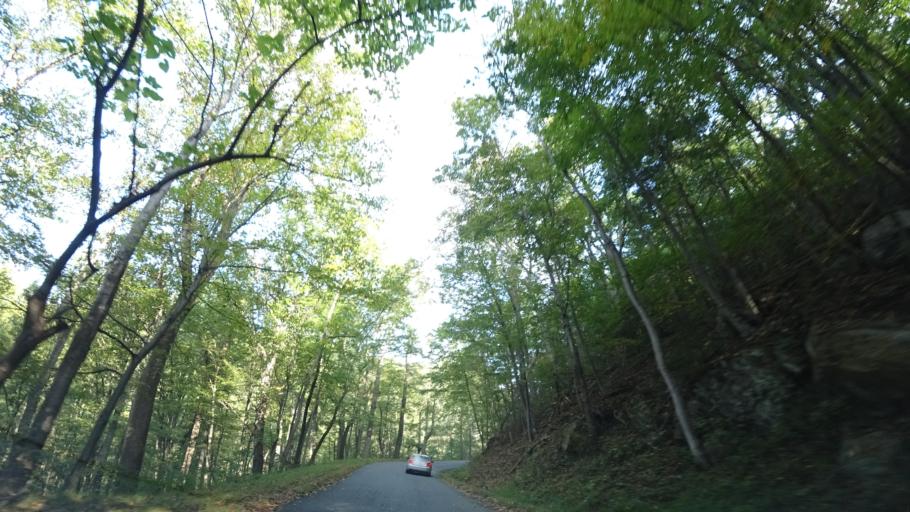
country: US
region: Virginia
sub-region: Madison County
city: Madison
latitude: 38.5060
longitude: -78.3121
